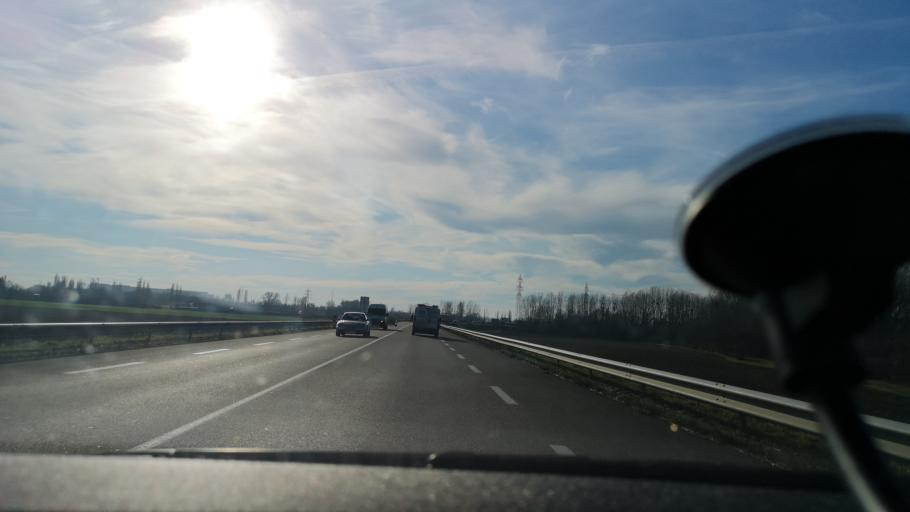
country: FR
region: Bourgogne
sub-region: Departement de Saone-et-Loire
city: Saint-Marcel
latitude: 46.7818
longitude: 4.8855
